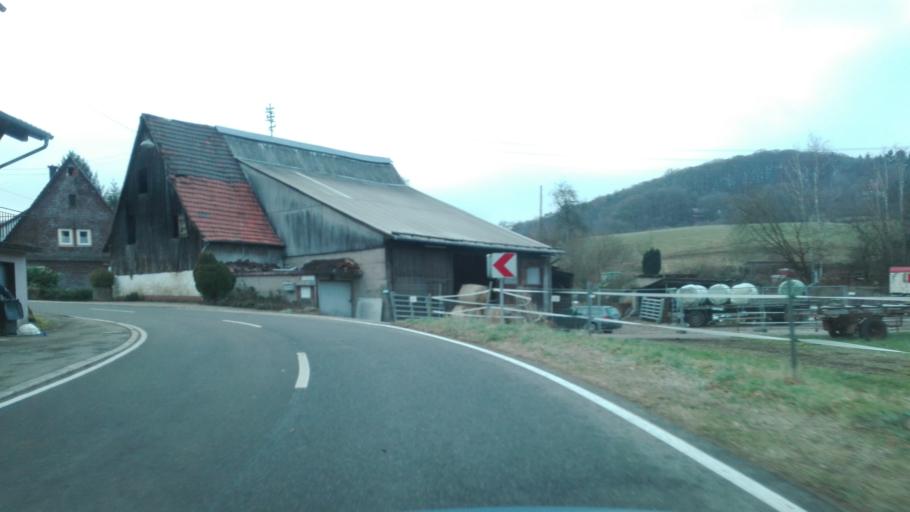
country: DE
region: Hesse
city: Unter-Abtsteinach
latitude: 49.5045
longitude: 8.7694
